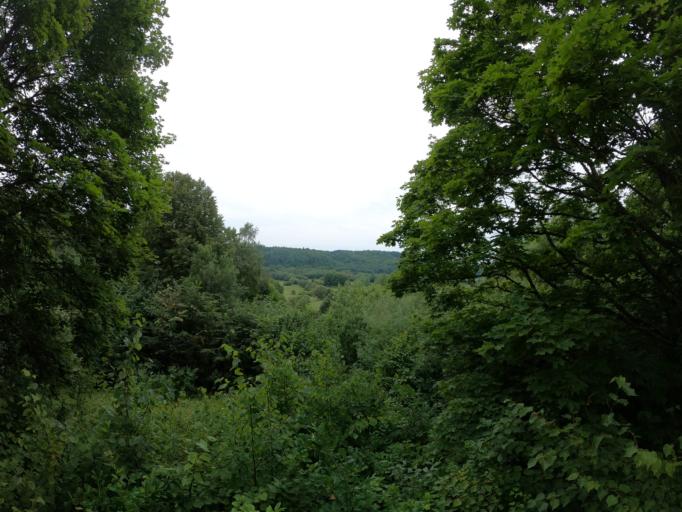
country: LT
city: Ariogala
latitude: 55.3160
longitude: 23.3614
